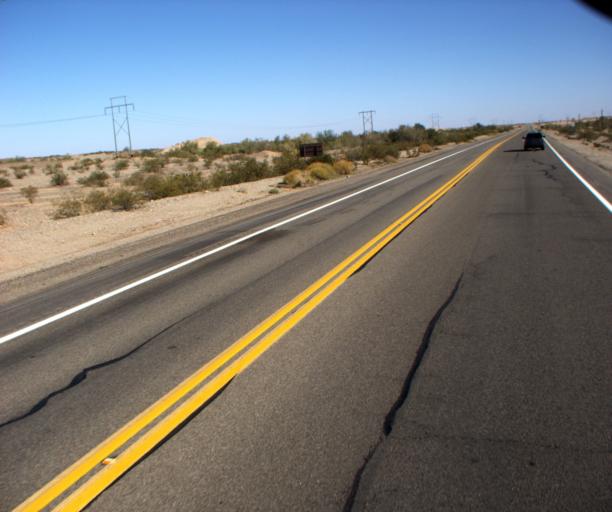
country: US
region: Arizona
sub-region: Yuma County
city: Fortuna Foothills
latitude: 32.7938
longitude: -114.3814
